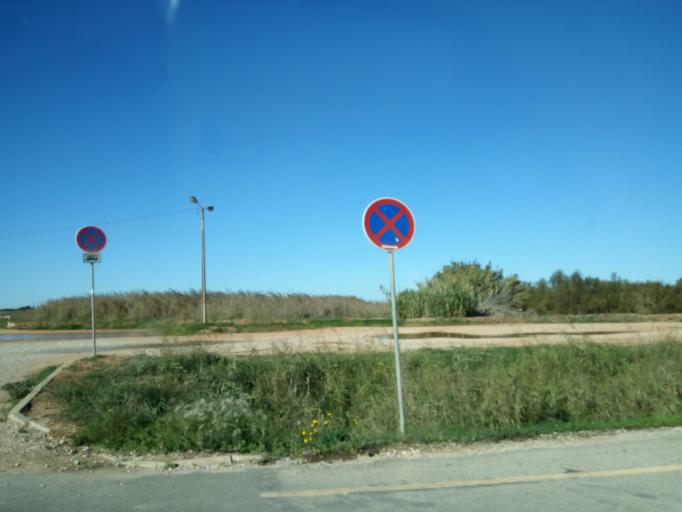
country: PT
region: Faro
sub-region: Loule
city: Vilamoura
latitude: 37.0783
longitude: -8.1280
